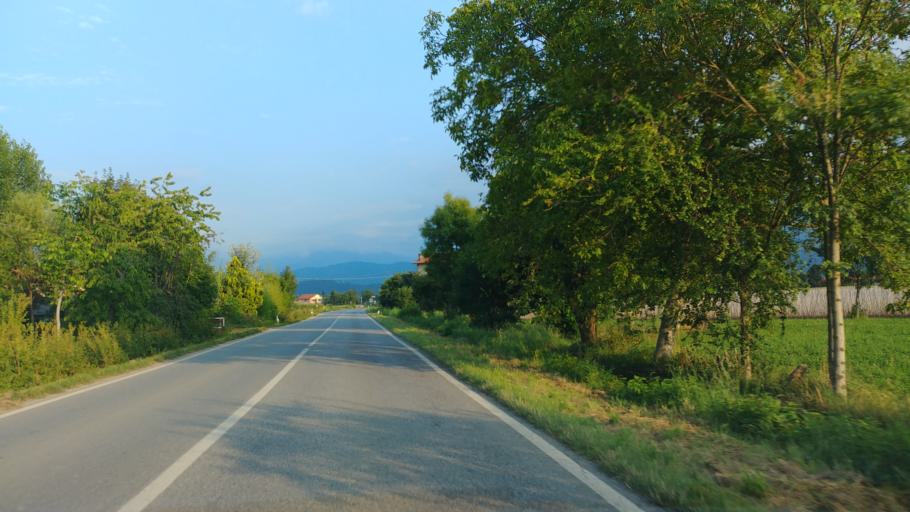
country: IT
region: Piedmont
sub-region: Provincia di Cuneo
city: Cuneo
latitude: 44.3661
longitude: 7.5822
